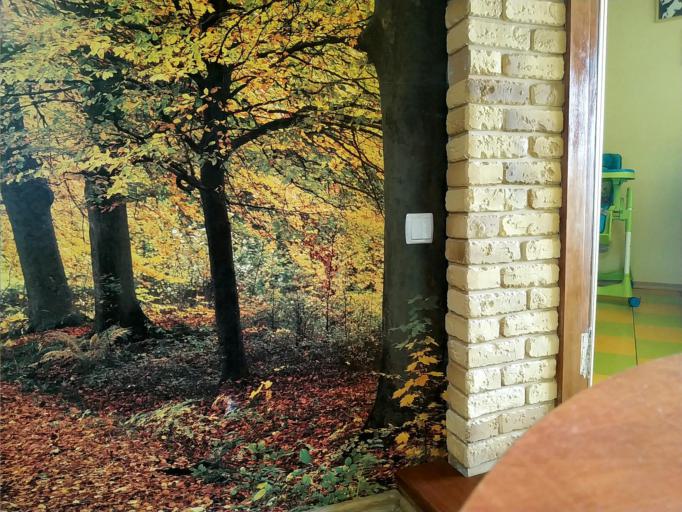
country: RU
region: Smolensk
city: Ozernyy
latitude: 55.4469
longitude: 32.6626
